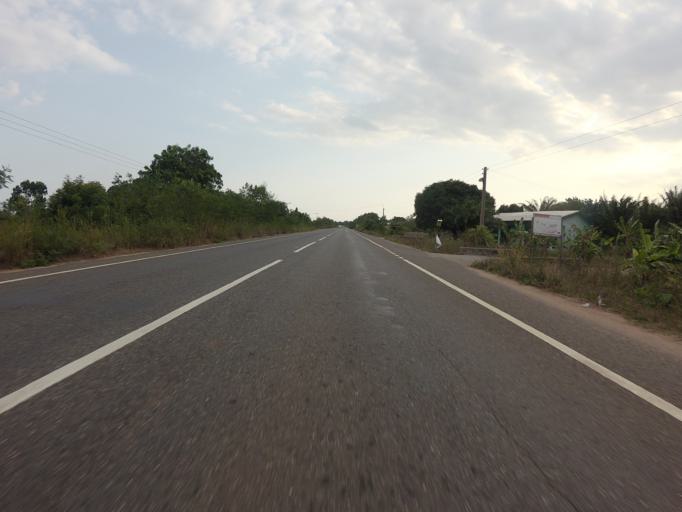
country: GH
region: Volta
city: Anloga
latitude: 6.1006
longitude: 0.5112
